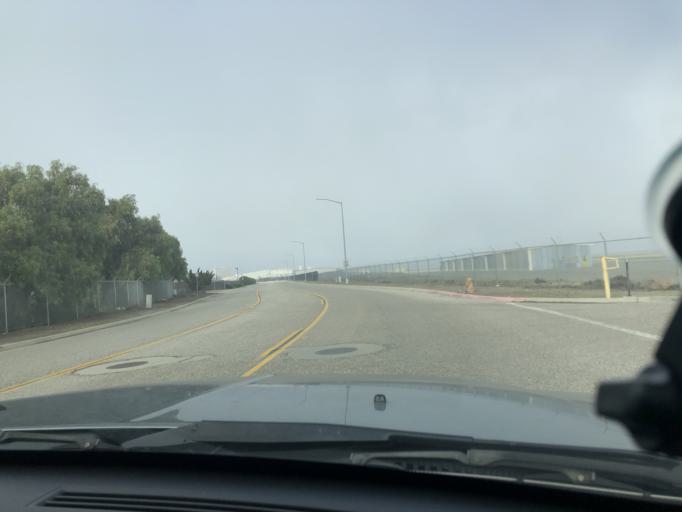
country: US
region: California
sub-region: Monterey County
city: King City
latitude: 36.2252
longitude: -121.1187
